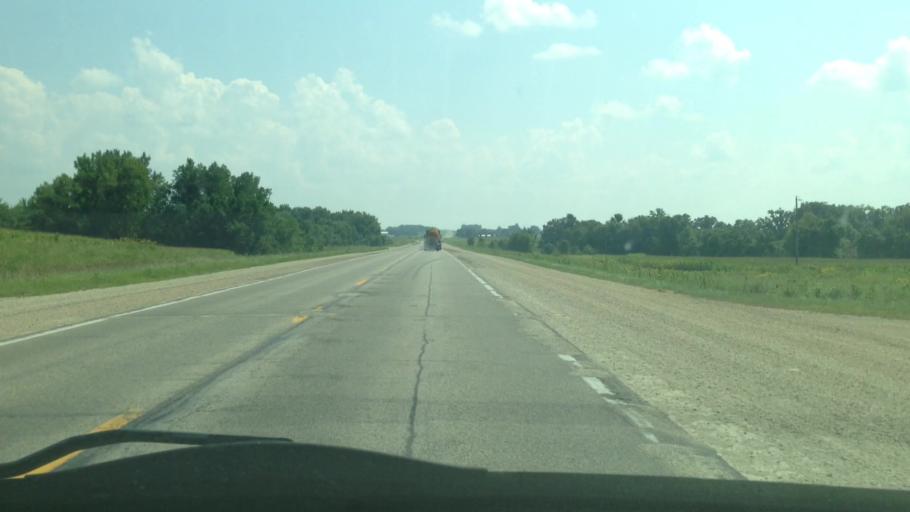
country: US
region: Iowa
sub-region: Chickasaw County
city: New Hampton
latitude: 43.2442
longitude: -92.2991
